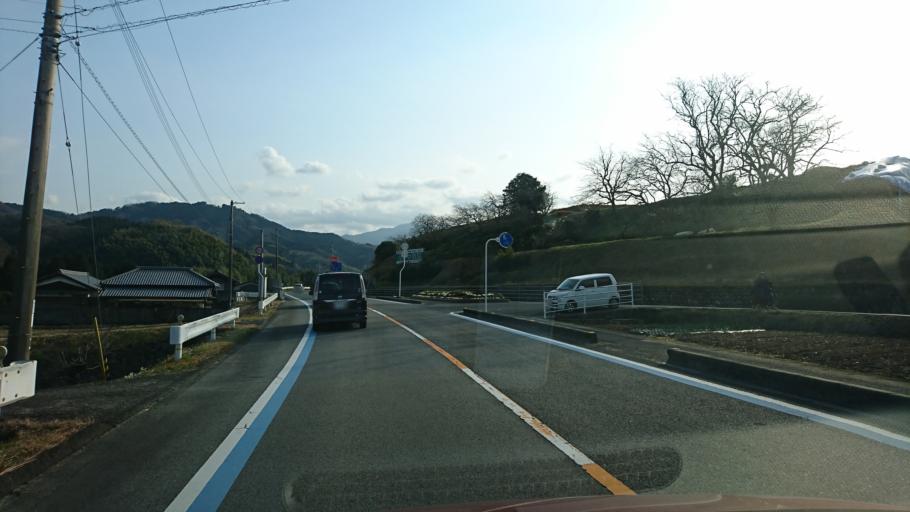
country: JP
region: Ehime
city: Hojo
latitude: 34.0060
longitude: 132.9384
